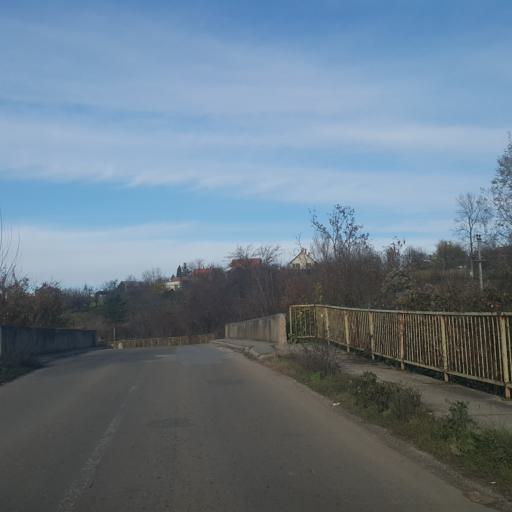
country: RS
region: Central Serbia
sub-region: Belgrade
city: Lazarevac
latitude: 44.3747
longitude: 20.4077
